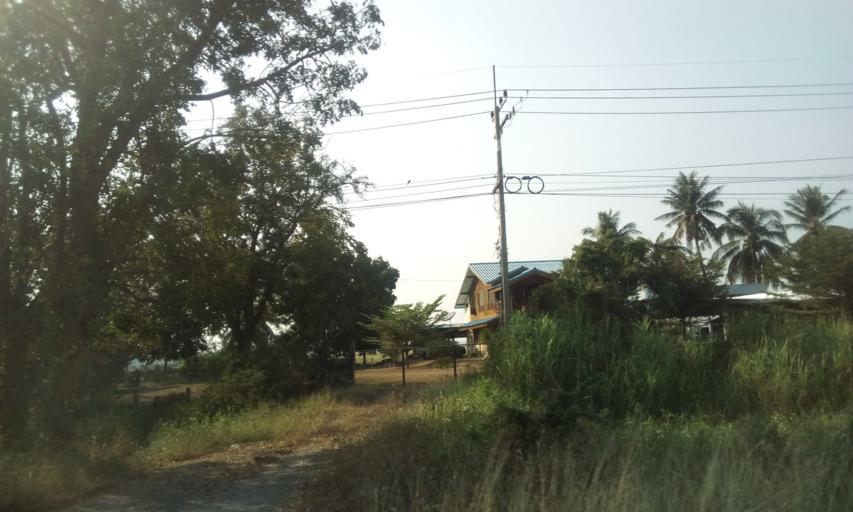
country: TH
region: Sing Buri
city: Phrom Buri
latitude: 14.7619
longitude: 100.4391
